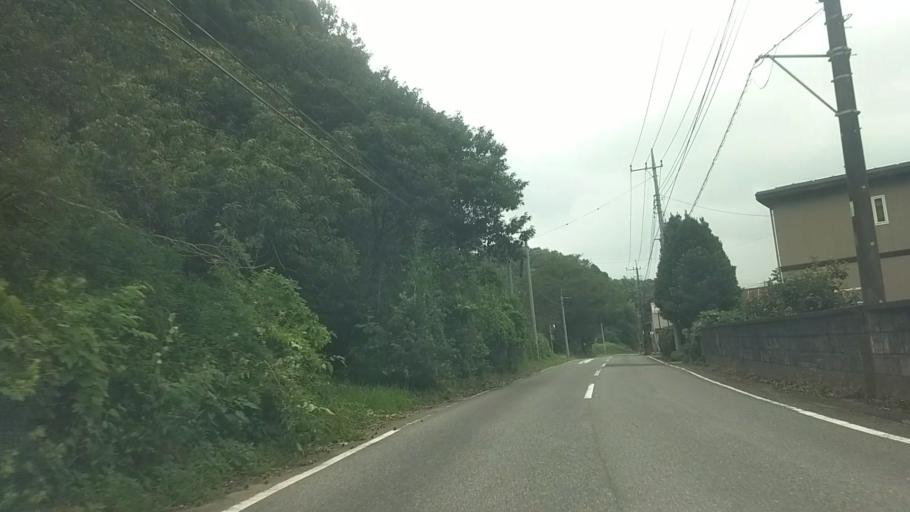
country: JP
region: Chiba
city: Kimitsu
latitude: 35.2359
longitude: 140.0034
